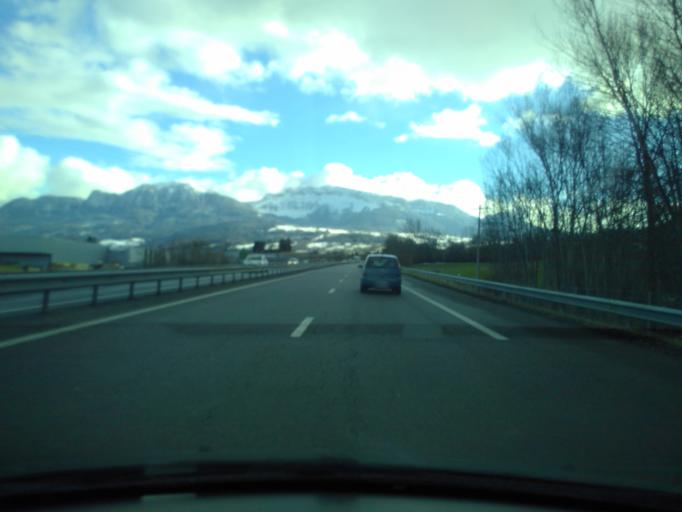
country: FR
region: Rhone-Alpes
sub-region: Departement de la Haute-Savoie
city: Cornier
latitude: 46.0802
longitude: 6.2893
